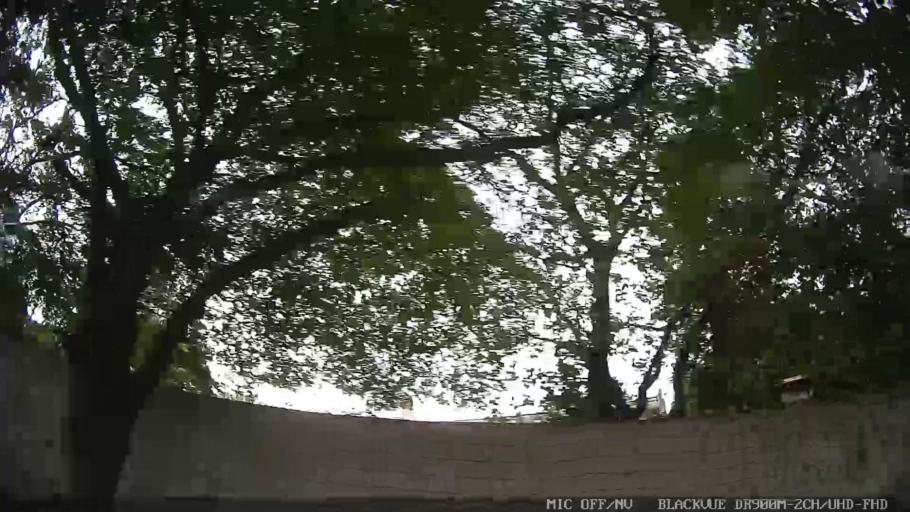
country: BR
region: Sao Paulo
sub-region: Braganca Paulista
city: Braganca Paulista
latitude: -22.9580
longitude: -46.5459
